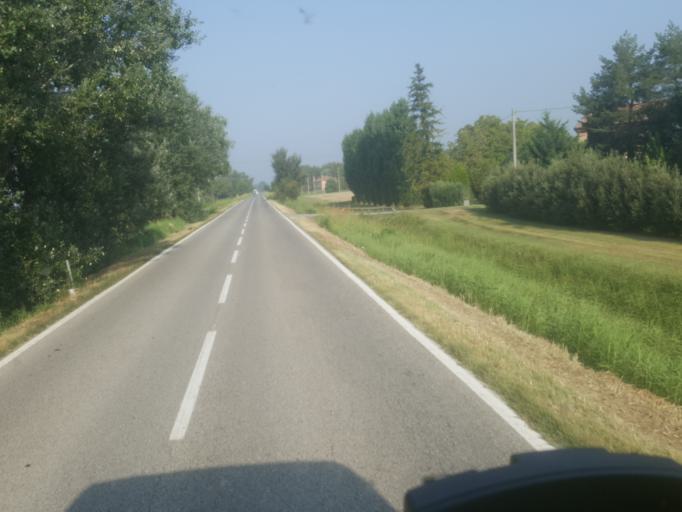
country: IT
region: Emilia-Romagna
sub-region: Provincia di Ravenna
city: Lavezzola
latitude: 44.5657
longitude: 11.8988
